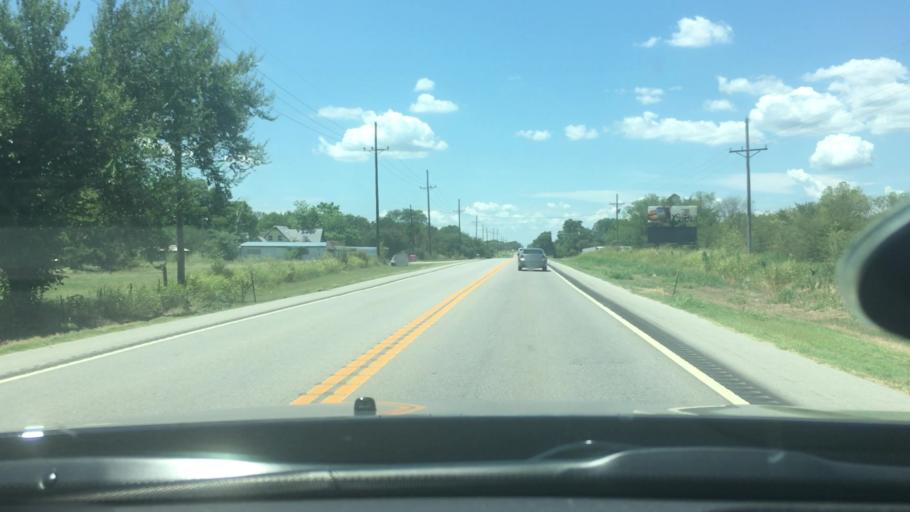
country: US
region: Oklahoma
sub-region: Bryan County
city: Durant
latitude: 33.9975
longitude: -96.3170
